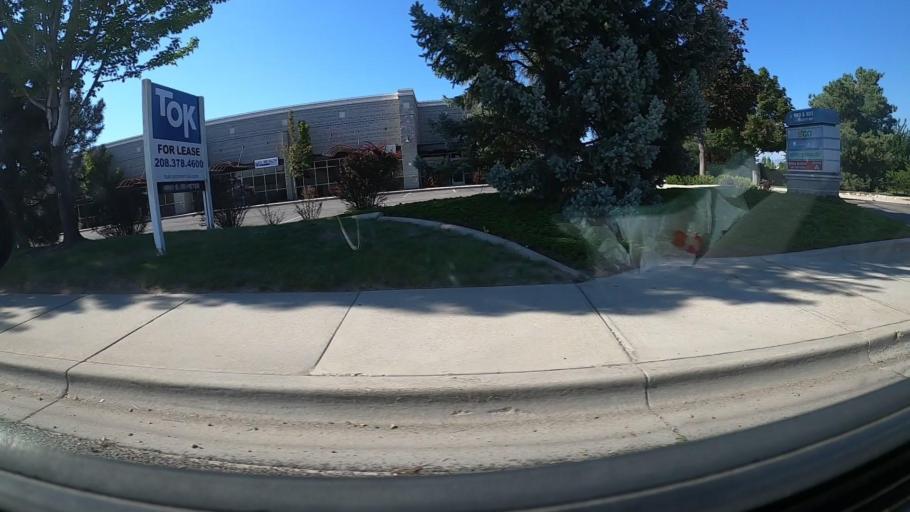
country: US
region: Idaho
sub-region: Ada County
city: Meridian
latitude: 43.5967
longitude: -116.3852
